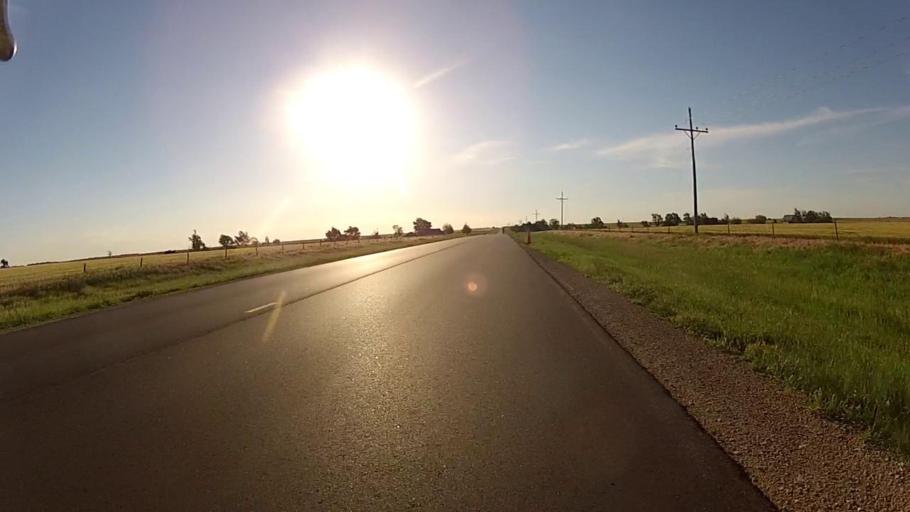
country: US
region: Kansas
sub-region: Comanche County
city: Coldwater
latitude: 37.2815
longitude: -99.1765
